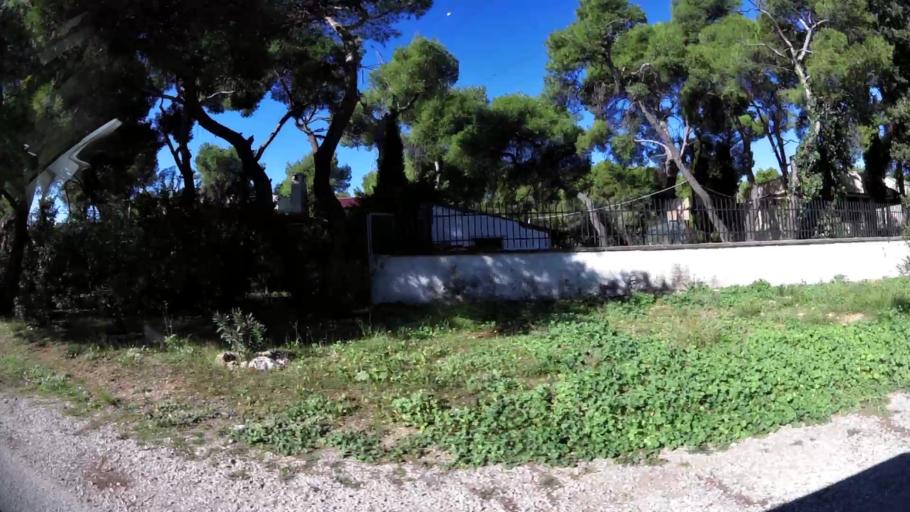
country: GR
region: Attica
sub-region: Nomarchia Anatolikis Attikis
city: Varybobi
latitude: 38.1280
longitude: 23.7891
